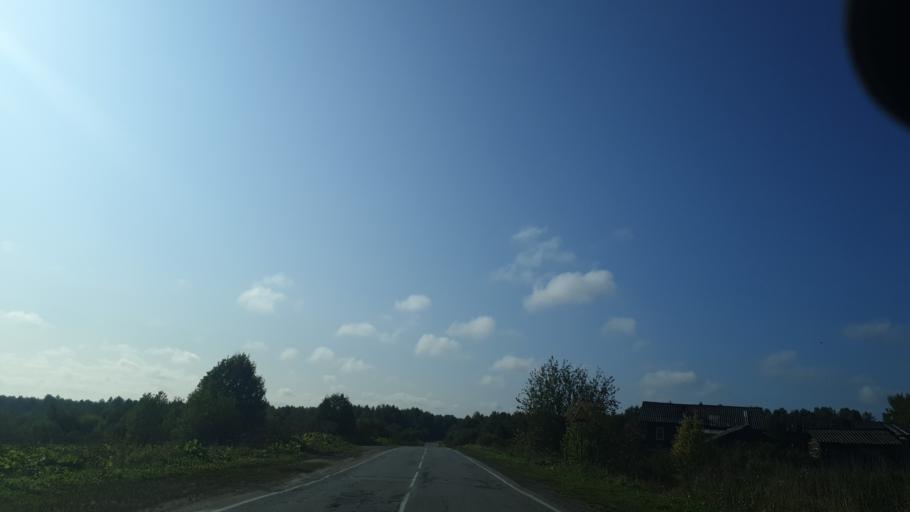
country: RU
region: Komi Republic
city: Vizinga
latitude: 60.7909
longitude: 50.1934
